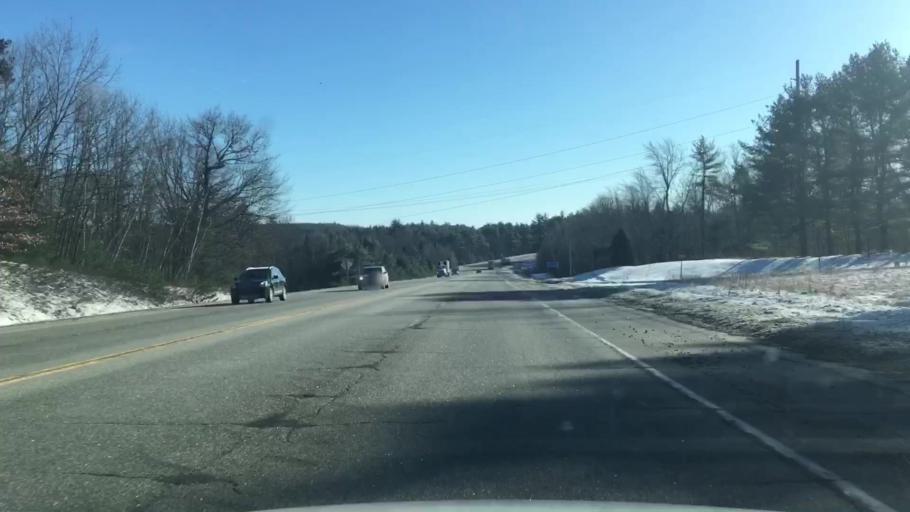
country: US
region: Maine
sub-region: Androscoggin County
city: Turner
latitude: 44.1833
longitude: -70.2345
